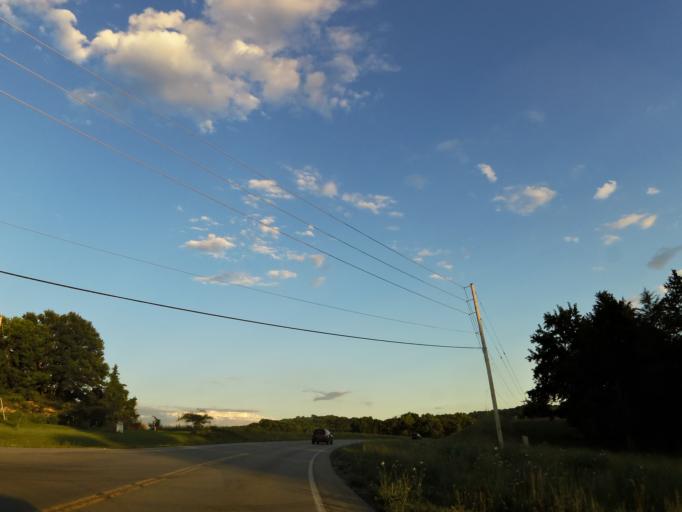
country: US
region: Missouri
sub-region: Jefferson County
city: Cedar Hill
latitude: 38.3394
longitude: -90.6475
